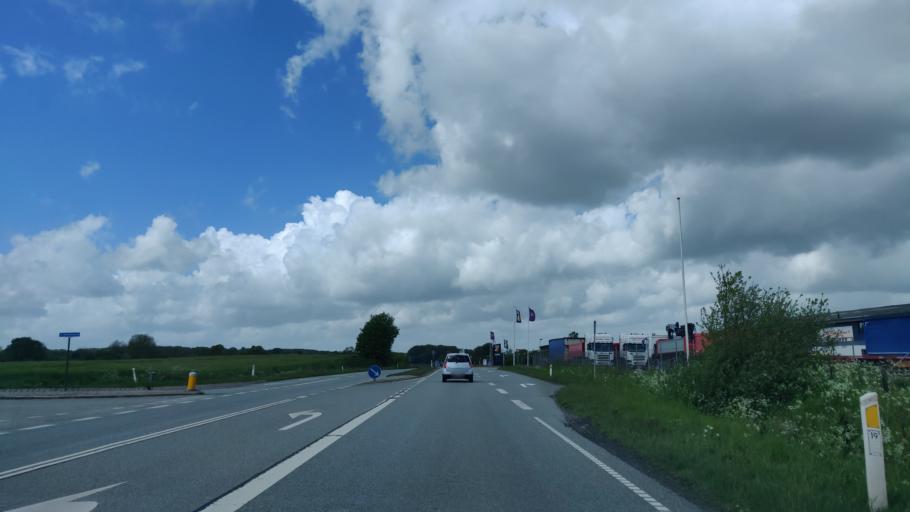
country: DK
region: Central Jutland
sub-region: Hedensted Kommune
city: Torring
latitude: 55.8444
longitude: 9.4903
